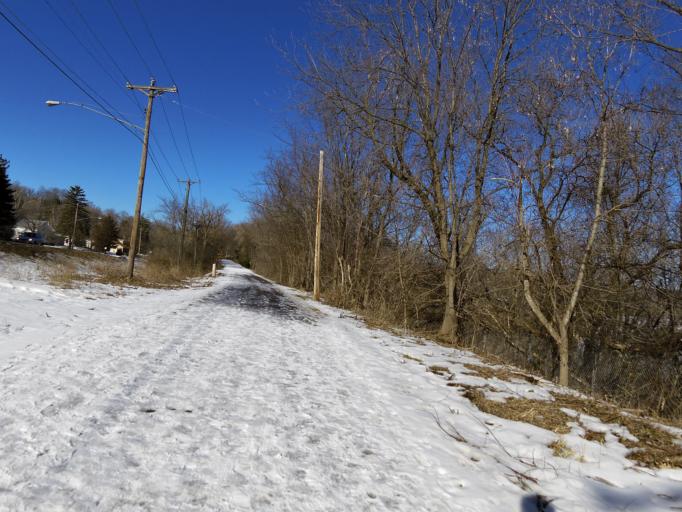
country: US
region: Minnesota
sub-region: Washington County
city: Stillwater
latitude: 45.0710
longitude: -92.8064
